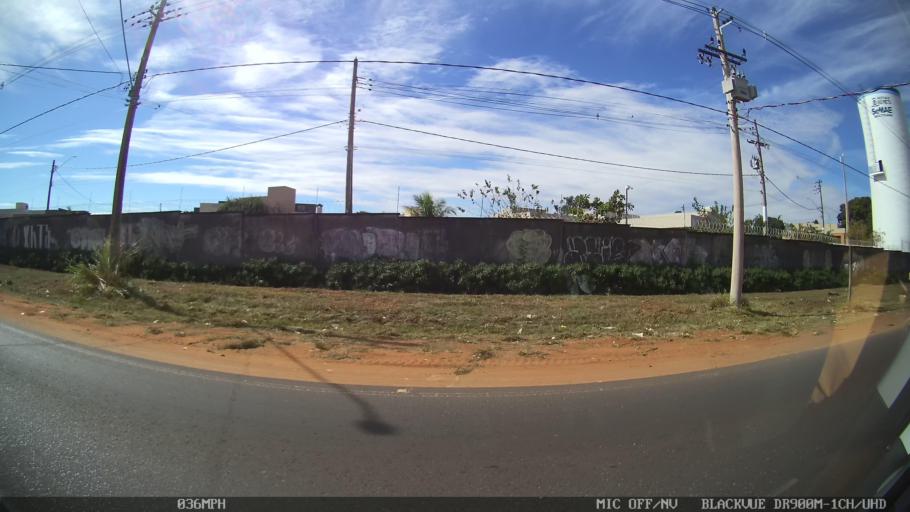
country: BR
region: Sao Paulo
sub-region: Sao Jose Do Rio Preto
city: Sao Jose do Rio Preto
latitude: -20.8352
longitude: -49.3373
